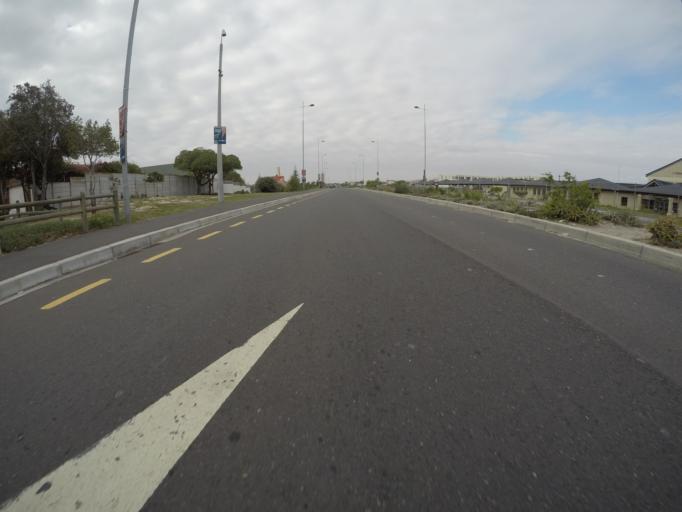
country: ZA
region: Western Cape
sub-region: City of Cape Town
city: Sunset Beach
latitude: -33.7302
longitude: 18.4430
